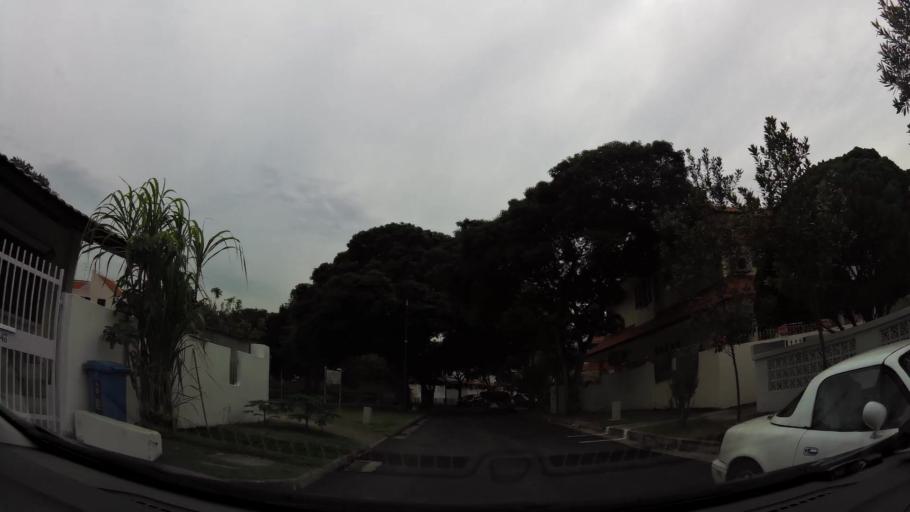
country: SG
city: Singapore
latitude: 1.3578
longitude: 103.8674
